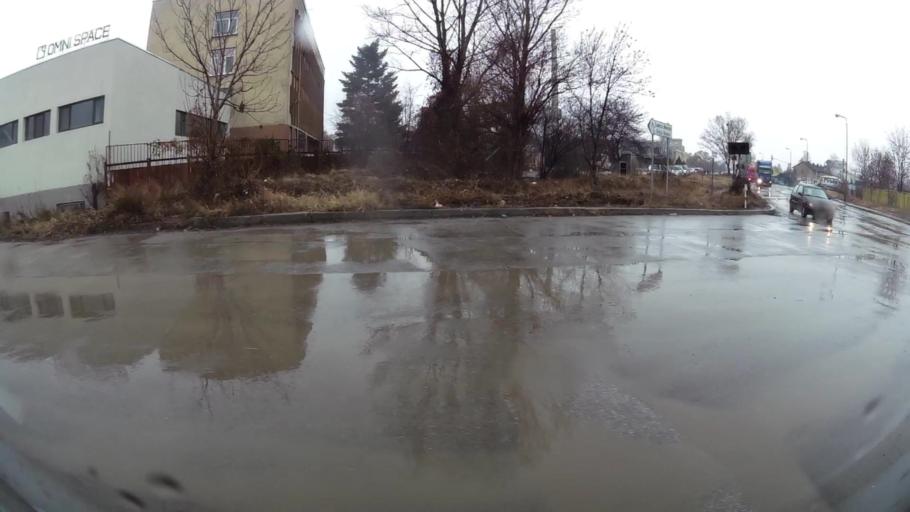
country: RO
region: Ilfov
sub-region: Comuna Corbeanca
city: Corbeanca
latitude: 44.5790
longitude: 26.0610
